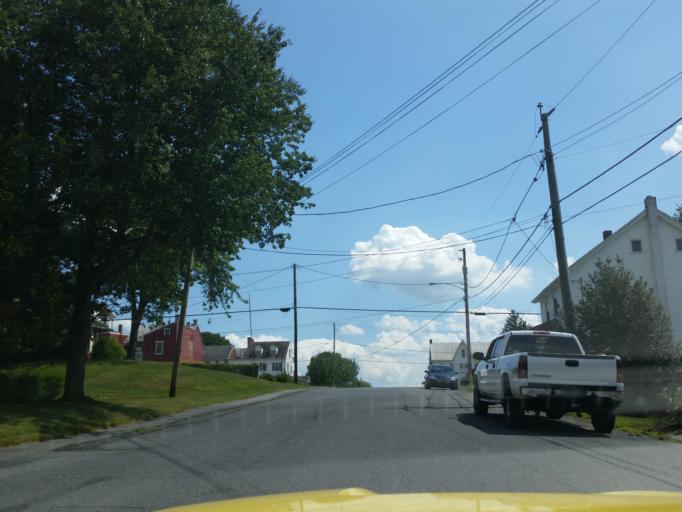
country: US
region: Pennsylvania
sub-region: Lebanon County
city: Jonestown
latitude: 40.4147
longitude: -76.4802
